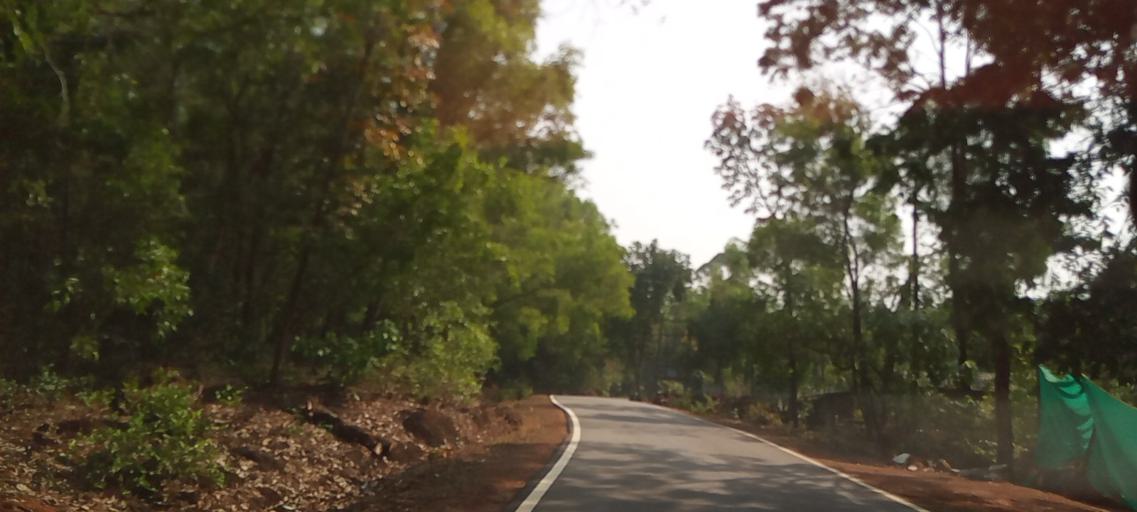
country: IN
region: Karnataka
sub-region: Udupi
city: Hosangadi
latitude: 13.5415
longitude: 74.9055
